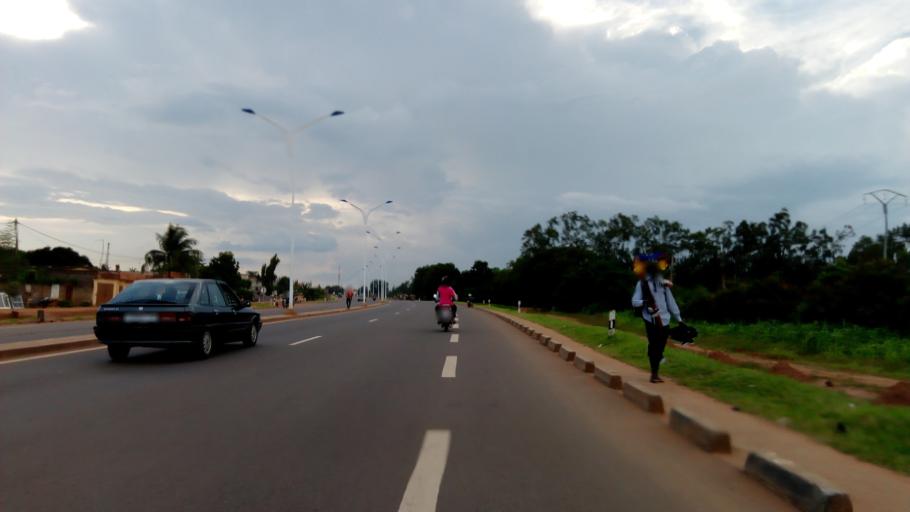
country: TG
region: Maritime
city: Lome
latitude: 6.2444
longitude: 1.1918
